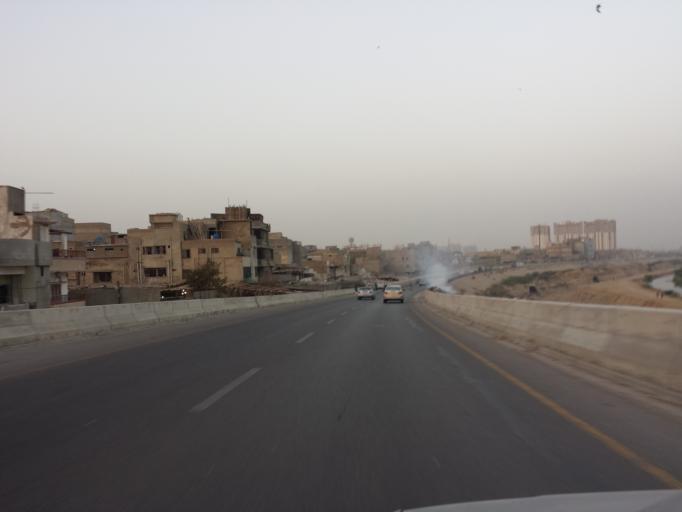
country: PK
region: Sindh
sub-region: Karachi District
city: Karachi
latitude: 24.9092
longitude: 67.0649
